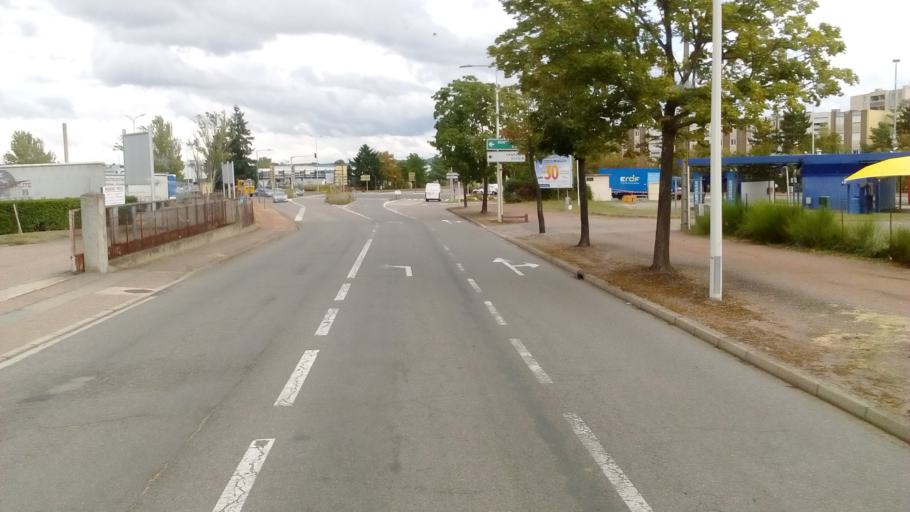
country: FR
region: Rhone-Alpes
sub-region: Departement de la Loire
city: Le Coteau
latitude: 46.0593
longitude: 4.0865
